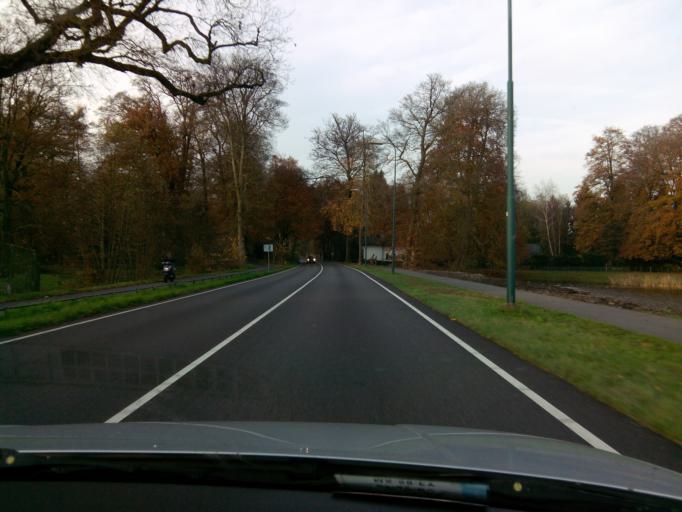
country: NL
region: Utrecht
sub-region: Gemeente Amersfoort
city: Randenbroek
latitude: 52.1386
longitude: 5.4104
